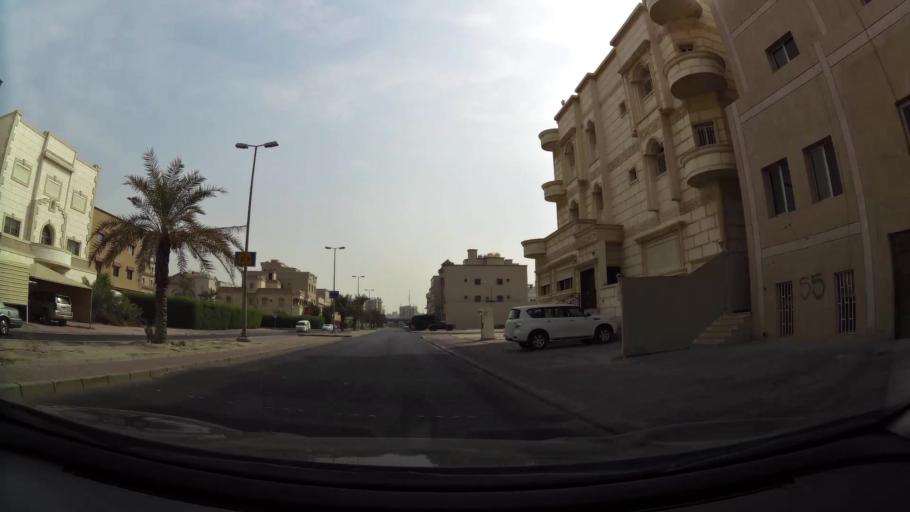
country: KW
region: Al Farwaniyah
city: Al Farwaniyah
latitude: 29.2712
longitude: 47.9396
